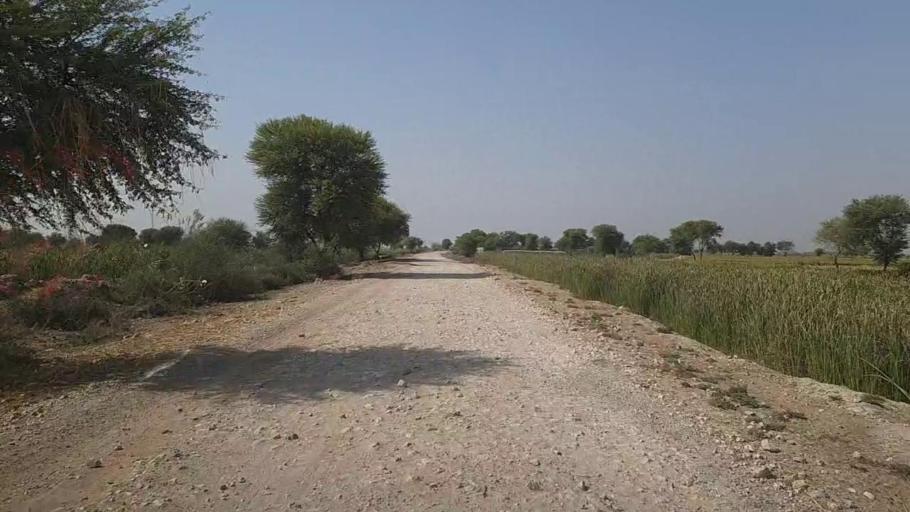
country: PK
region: Sindh
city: Kandhkot
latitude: 28.3936
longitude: 69.2784
